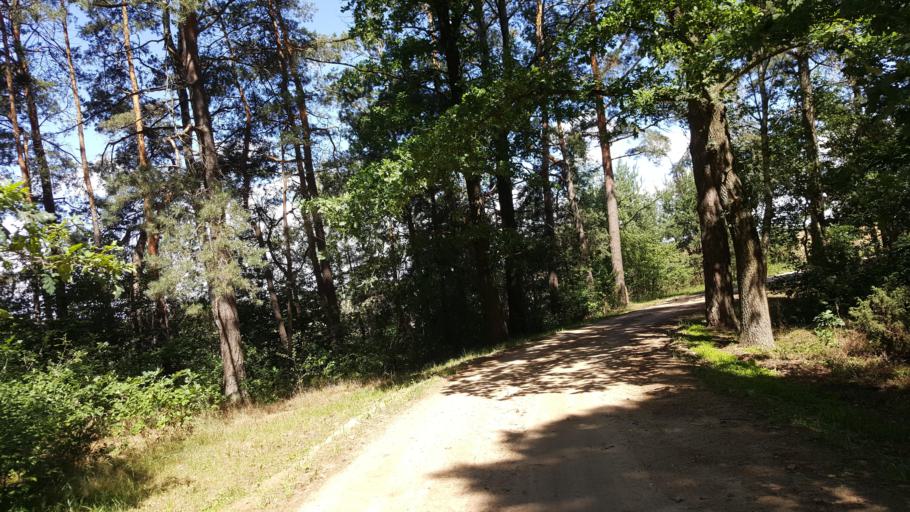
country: BY
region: Brest
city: Kamyanyets
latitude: 52.3294
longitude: 23.9016
